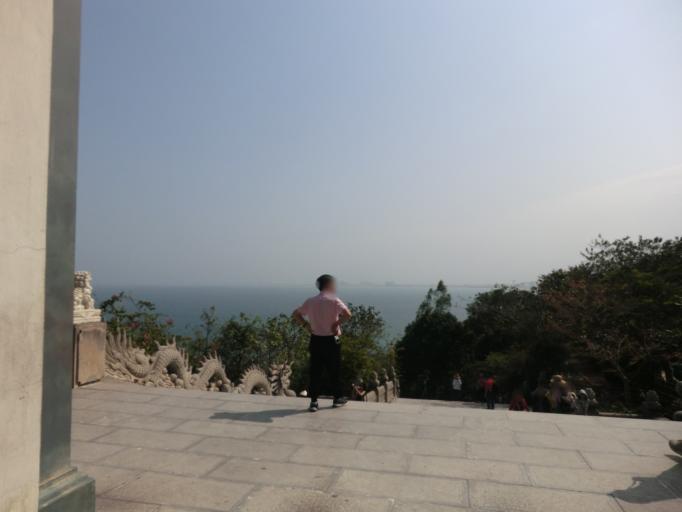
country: VN
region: Da Nang
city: Son Tra
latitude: 16.0996
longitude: 108.2776
